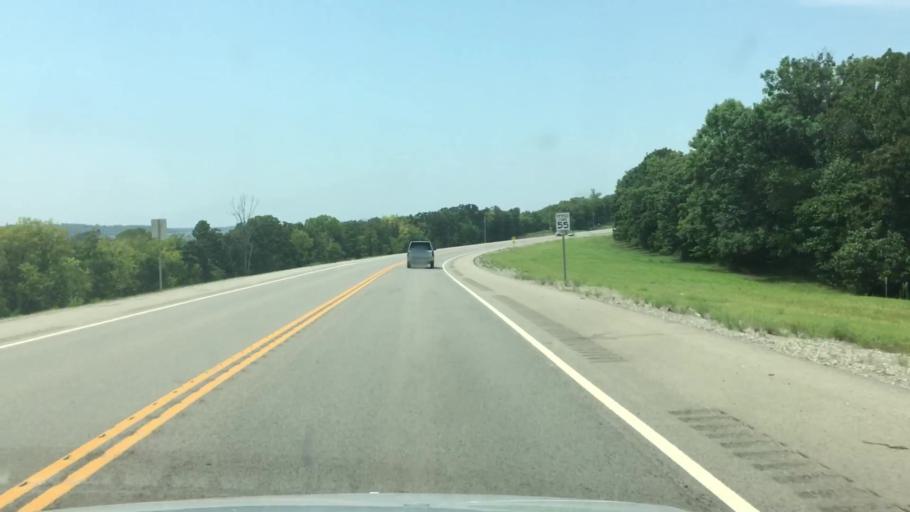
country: US
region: Oklahoma
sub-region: Wagoner County
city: Wagoner
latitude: 35.9287
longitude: -95.2574
